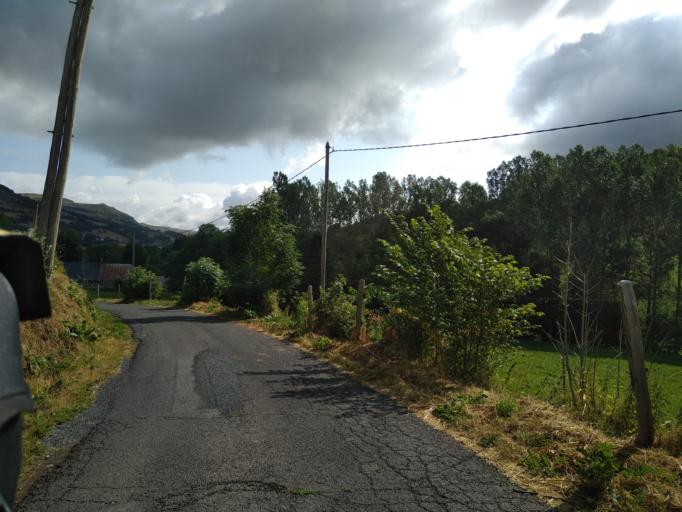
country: FR
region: Auvergne
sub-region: Departement du Cantal
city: Murat
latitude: 45.1275
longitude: 2.7408
